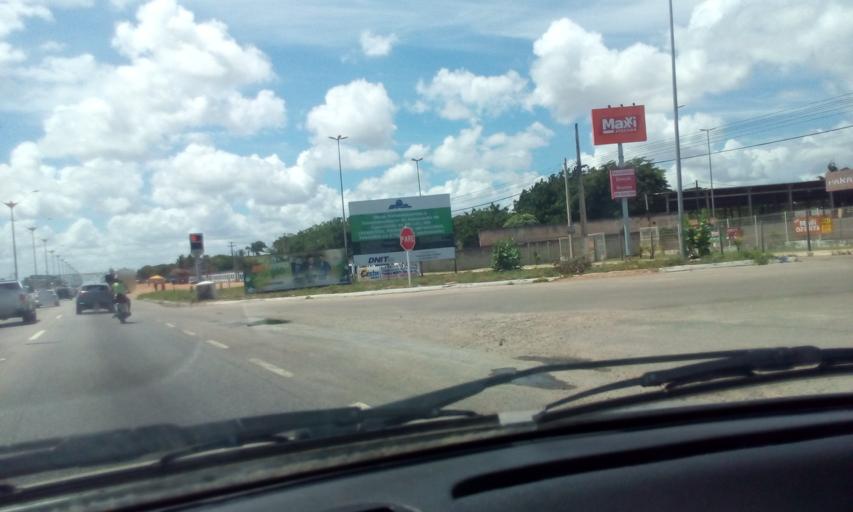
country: BR
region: Rio Grande do Norte
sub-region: Parnamirim
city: Parnamirim
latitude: -5.9018
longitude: -35.2595
